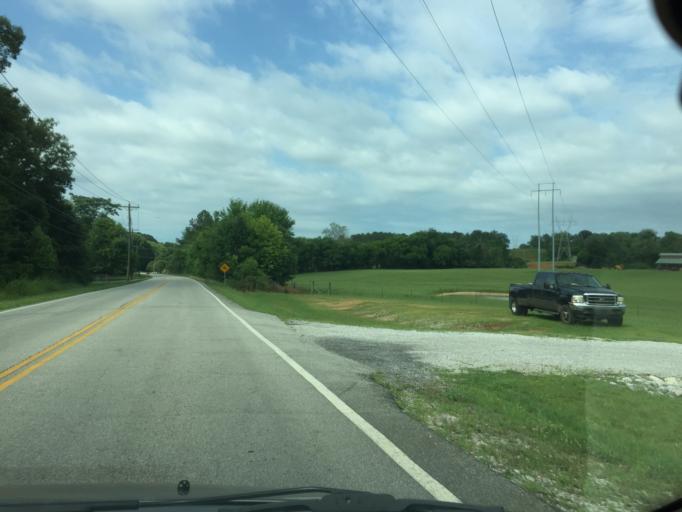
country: US
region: Tennessee
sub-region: Hamilton County
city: Apison
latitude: 35.0069
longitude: -85.0471
